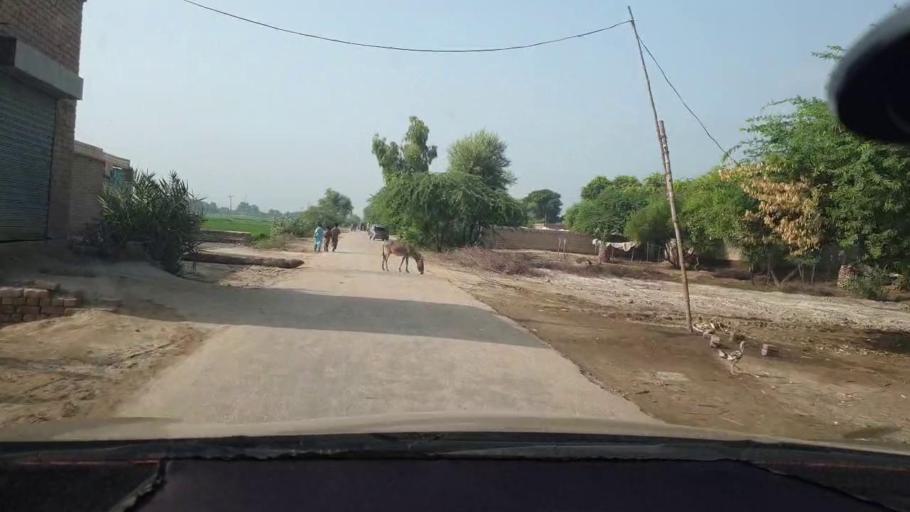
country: PK
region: Sindh
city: Kambar
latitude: 27.5031
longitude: 68.0132
